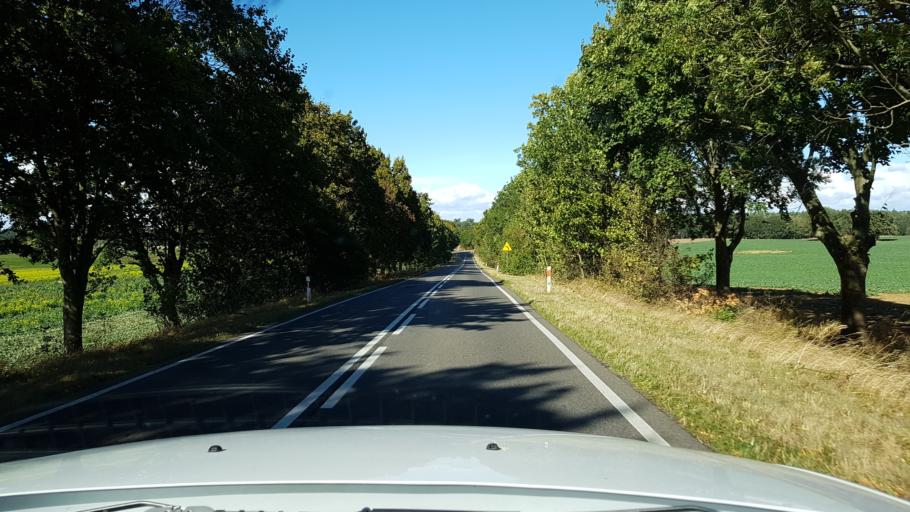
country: PL
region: West Pomeranian Voivodeship
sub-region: Powiat gryfinski
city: Banie
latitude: 53.1509
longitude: 14.6062
